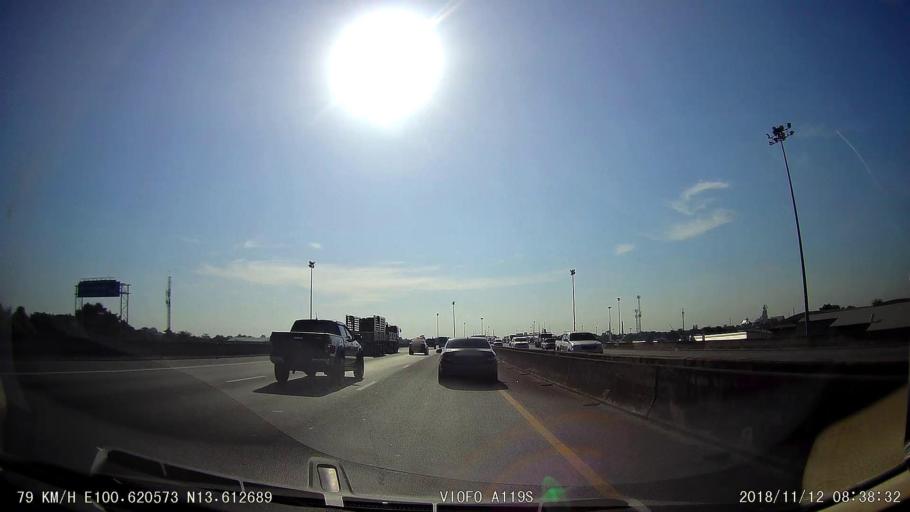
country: TH
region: Samut Prakan
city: Samut Prakan
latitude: 13.6125
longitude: 100.6208
